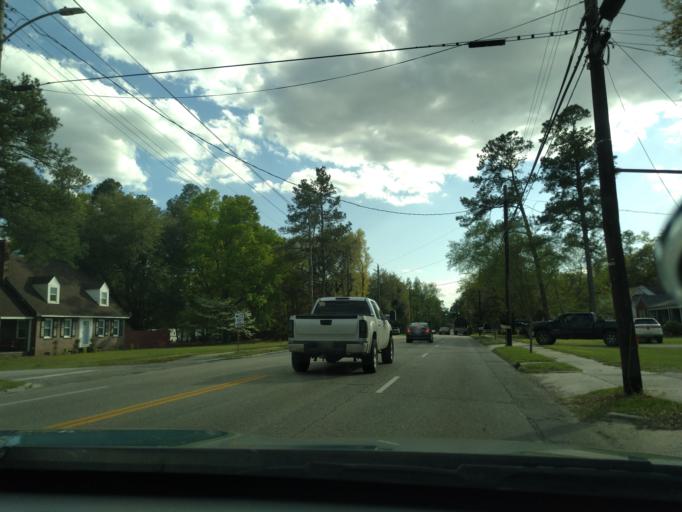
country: US
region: South Carolina
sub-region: Williamsburg County
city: Kingstree
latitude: 33.6776
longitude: -79.8308
